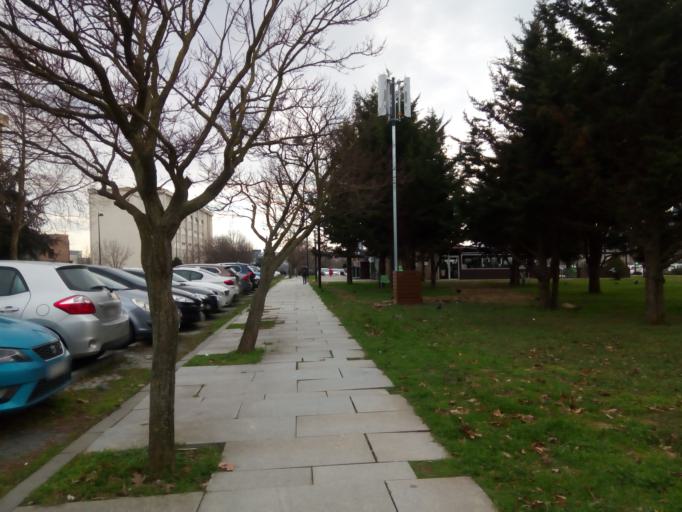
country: TR
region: Istanbul
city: Sisli
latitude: 41.1039
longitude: 29.0238
